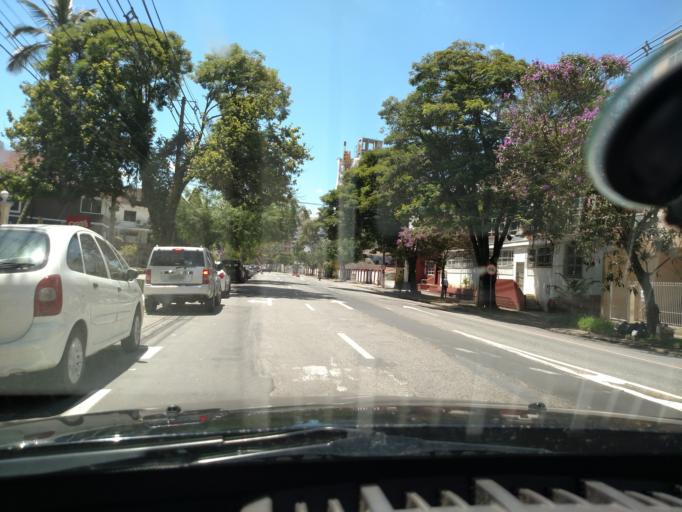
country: BR
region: Santa Catarina
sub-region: Blumenau
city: Blumenau
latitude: -26.9291
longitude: -49.0626
